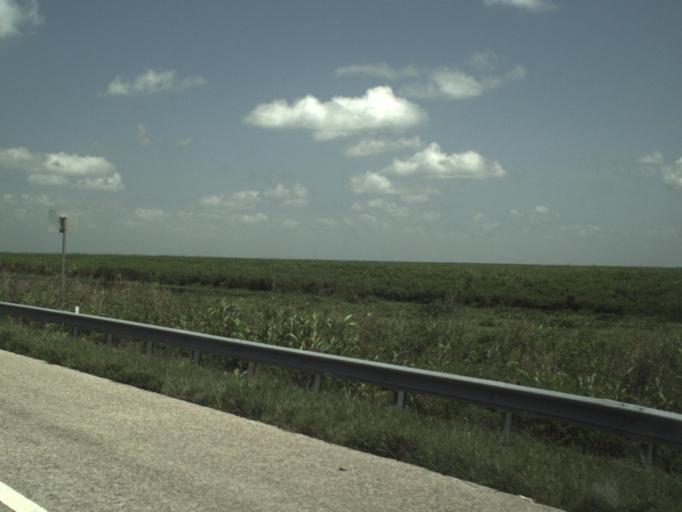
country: US
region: Florida
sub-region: Palm Beach County
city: Belle Glade Camp
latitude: 26.4456
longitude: -80.6233
